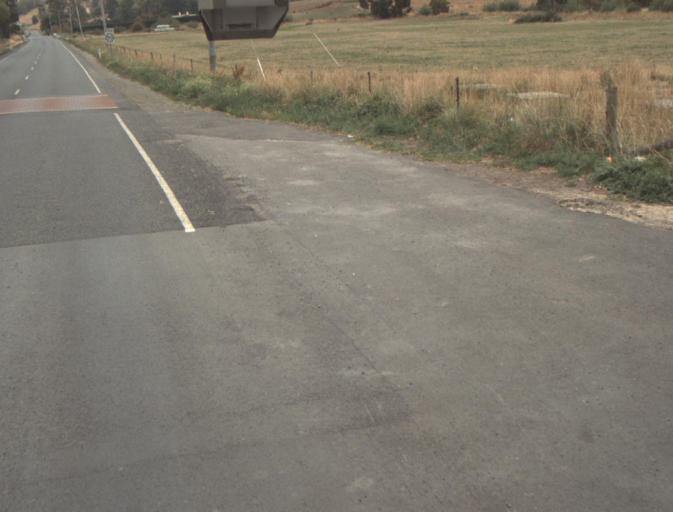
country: AU
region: Tasmania
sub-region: Launceston
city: Mayfield
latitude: -41.2480
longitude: 147.2177
